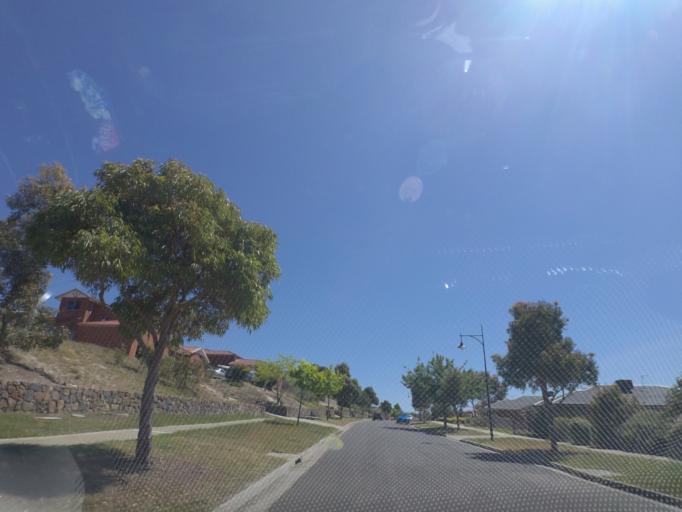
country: AU
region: Victoria
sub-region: Hume
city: Sunbury
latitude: -37.5564
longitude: 144.7115
